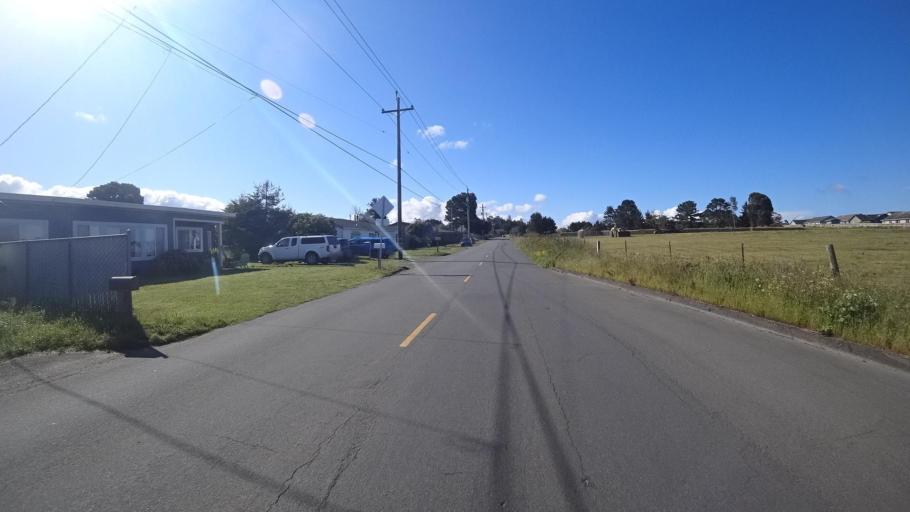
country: US
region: California
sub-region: Humboldt County
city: McKinleyville
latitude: 40.9372
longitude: -124.1078
